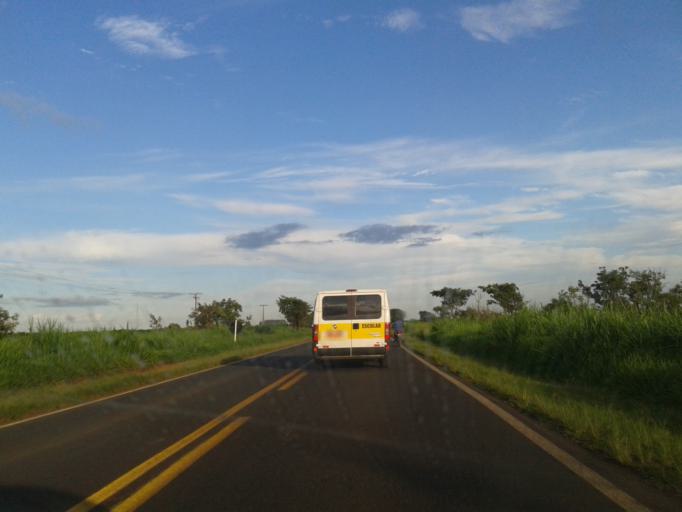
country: BR
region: Minas Gerais
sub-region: Araguari
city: Araguari
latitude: -18.6379
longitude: -48.2258
